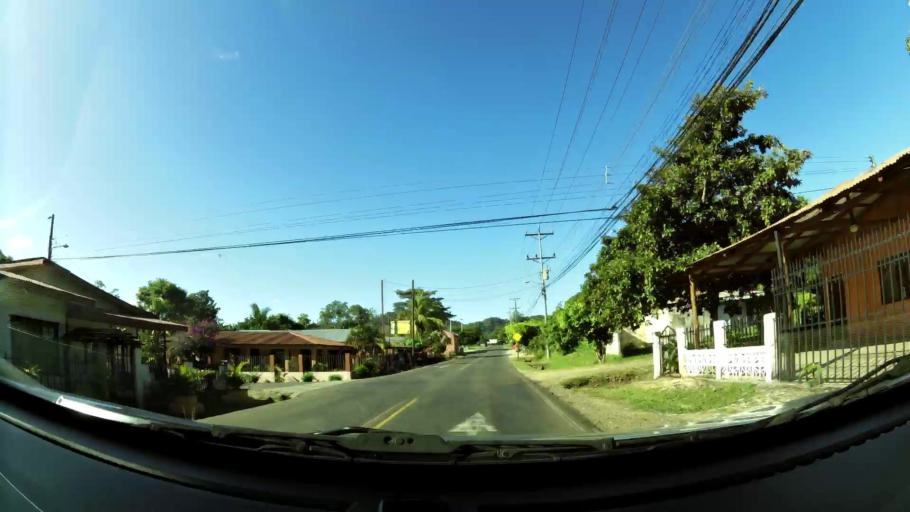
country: CR
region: Guanacaste
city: Belen
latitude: 10.3907
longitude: -85.6181
